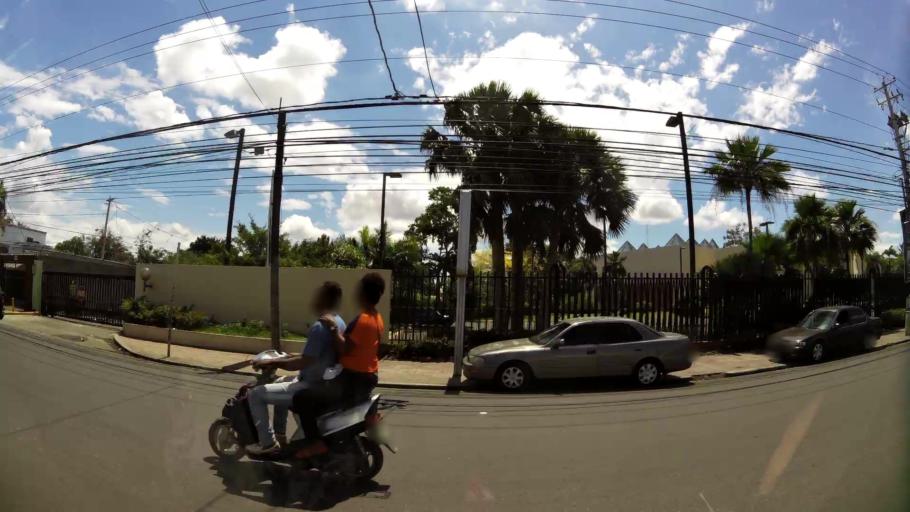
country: DO
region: Santiago
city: Santiago de los Caballeros
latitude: 19.4643
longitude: -70.6708
